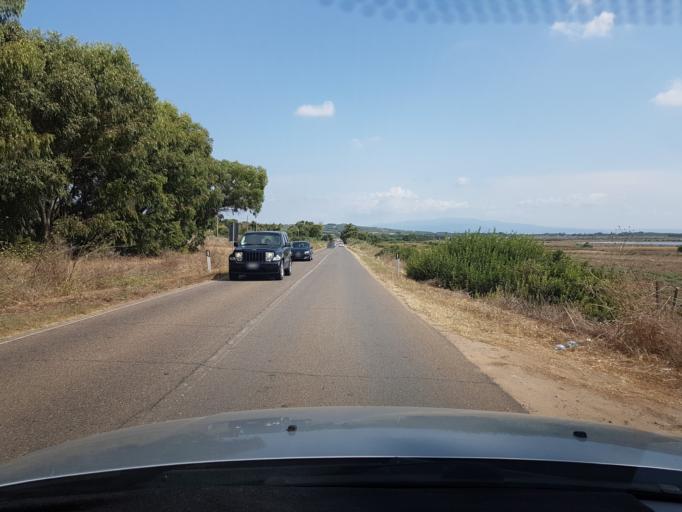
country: IT
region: Sardinia
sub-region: Provincia di Oristano
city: Cabras
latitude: 39.8987
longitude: 8.4347
